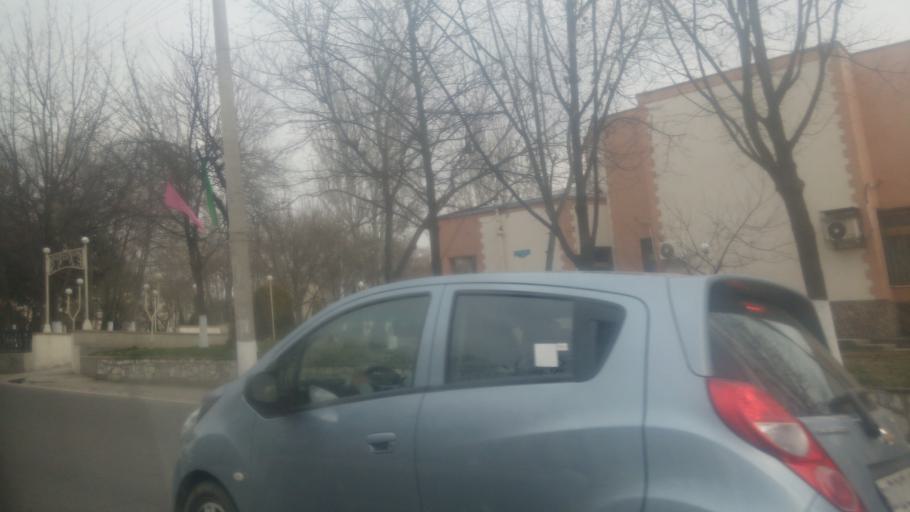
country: UZ
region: Toshkent
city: Salor
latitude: 41.3395
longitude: 69.3347
